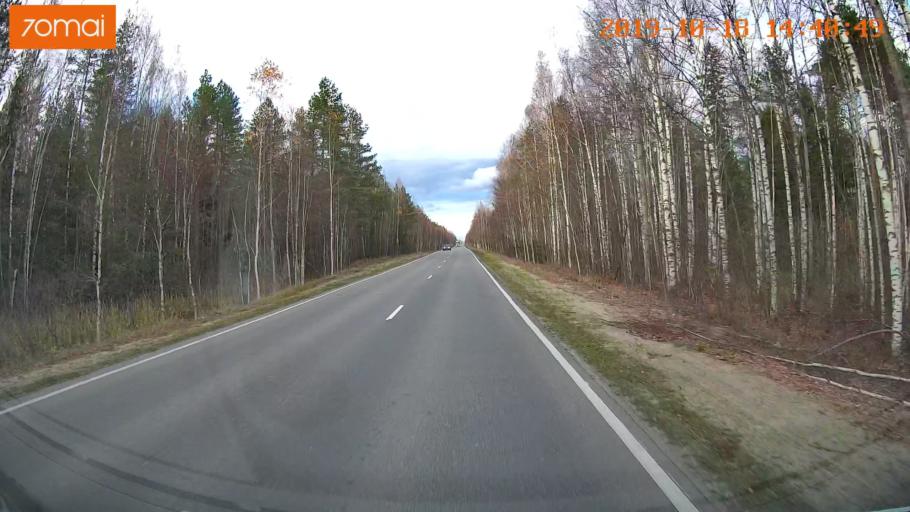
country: RU
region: Vladimir
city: Velikodvorskiy
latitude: 55.2824
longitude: 40.6697
